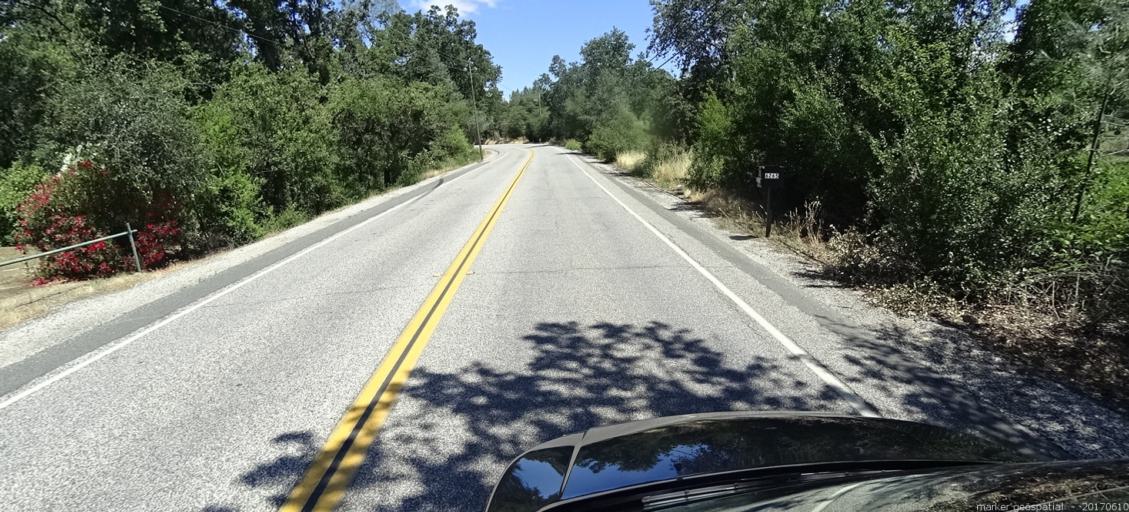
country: US
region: California
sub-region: Butte County
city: Oroville East
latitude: 39.4984
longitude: -121.4581
